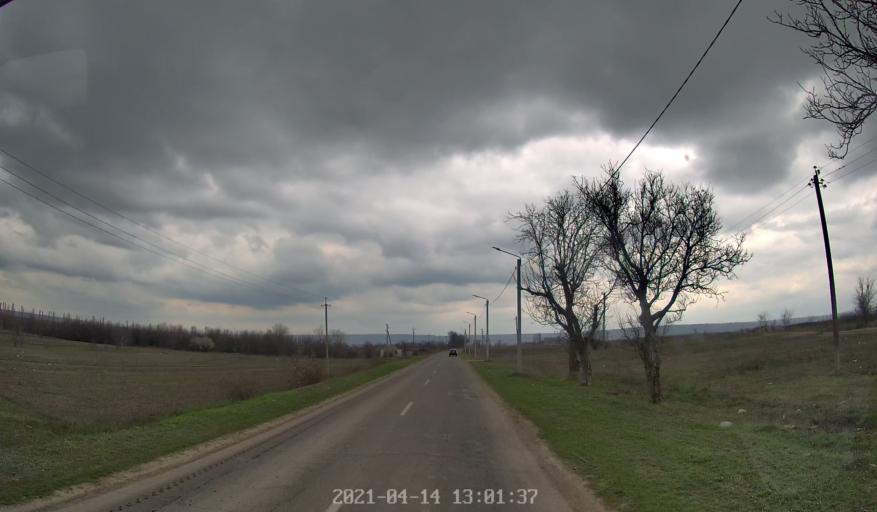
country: MD
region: Chisinau
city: Vadul lui Voda
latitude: 47.1302
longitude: 29.1152
